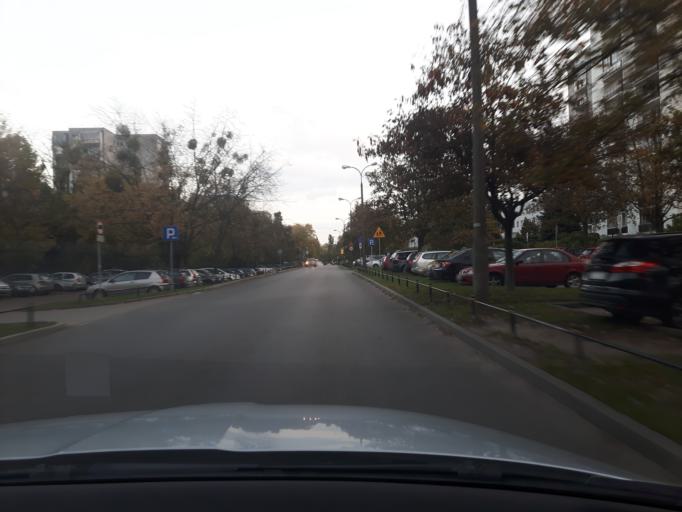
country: PL
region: Masovian Voivodeship
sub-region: Warszawa
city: Ursynow
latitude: 52.1420
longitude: 21.0505
